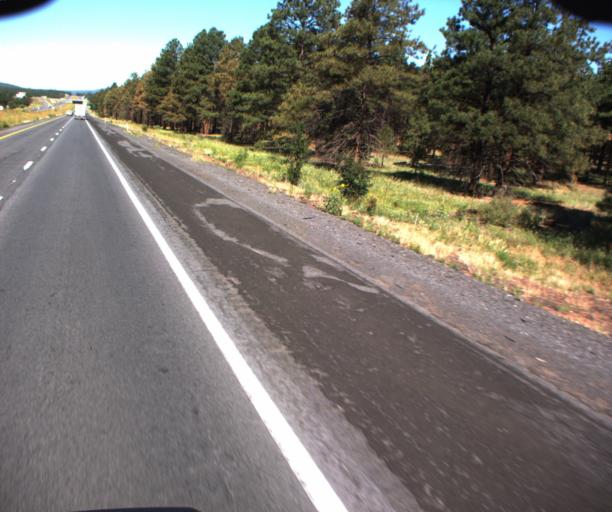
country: US
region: Arizona
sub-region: Coconino County
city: Williams
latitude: 35.2585
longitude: -112.1076
